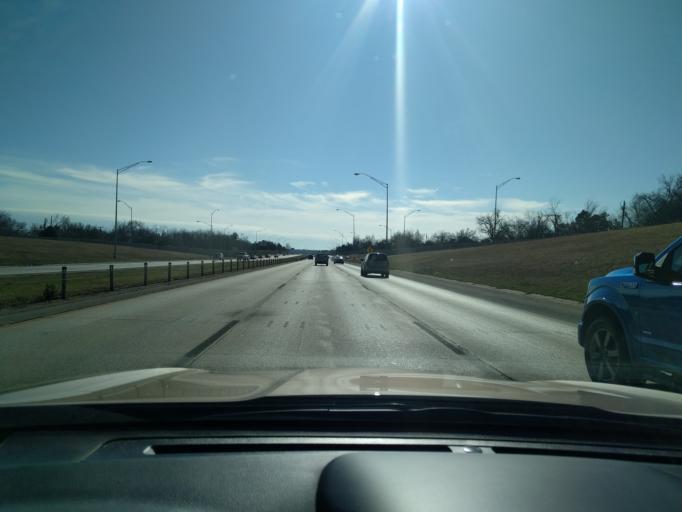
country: US
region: Oklahoma
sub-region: Oklahoma County
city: Nichols Hills
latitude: 35.5218
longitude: -97.5768
